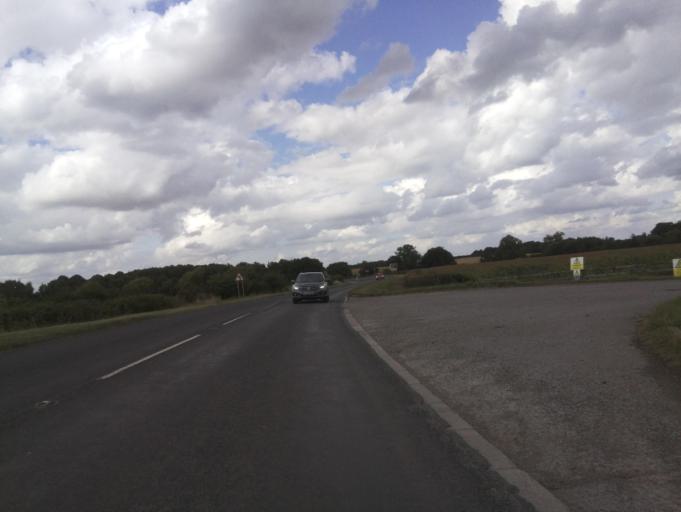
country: GB
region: England
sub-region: North Yorkshire
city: Ripon
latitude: 54.1740
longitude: -1.5532
